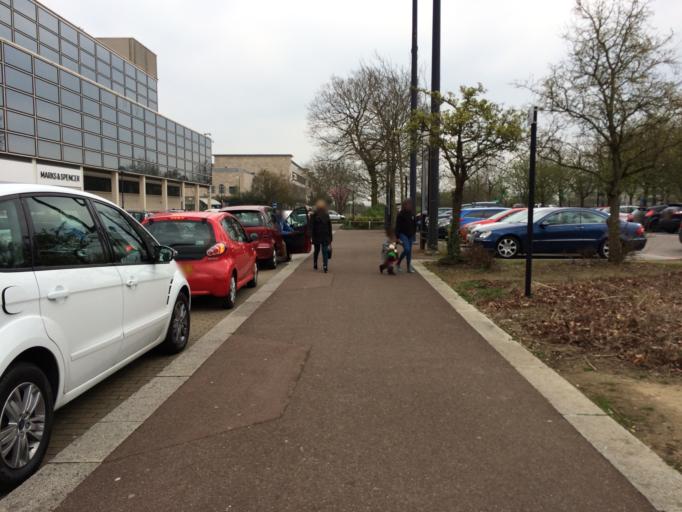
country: GB
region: England
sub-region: Milton Keynes
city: Milton Keynes
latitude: 52.0418
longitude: -0.7599
